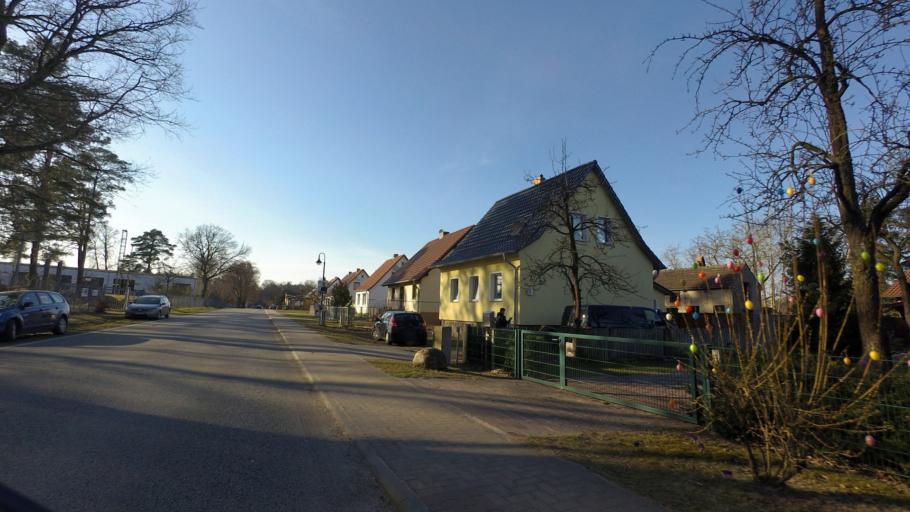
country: DE
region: Brandenburg
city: Althuttendorf
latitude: 52.9566
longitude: 13.7936
